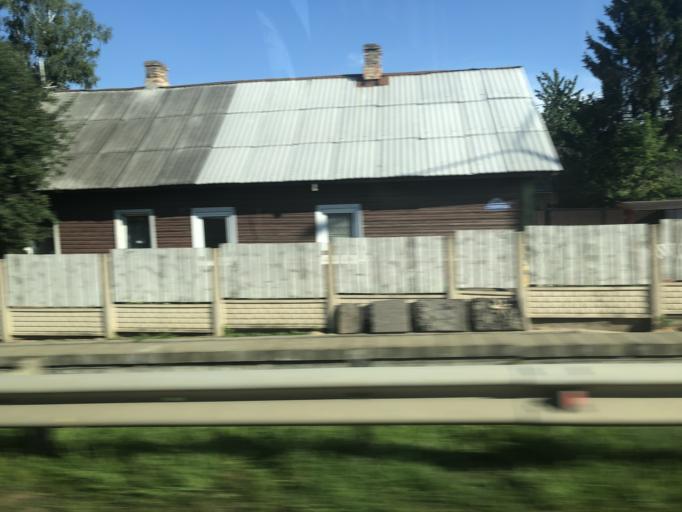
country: BY
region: Grodnenskaya
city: Hrodna
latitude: 53.6547
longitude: 23.7980
